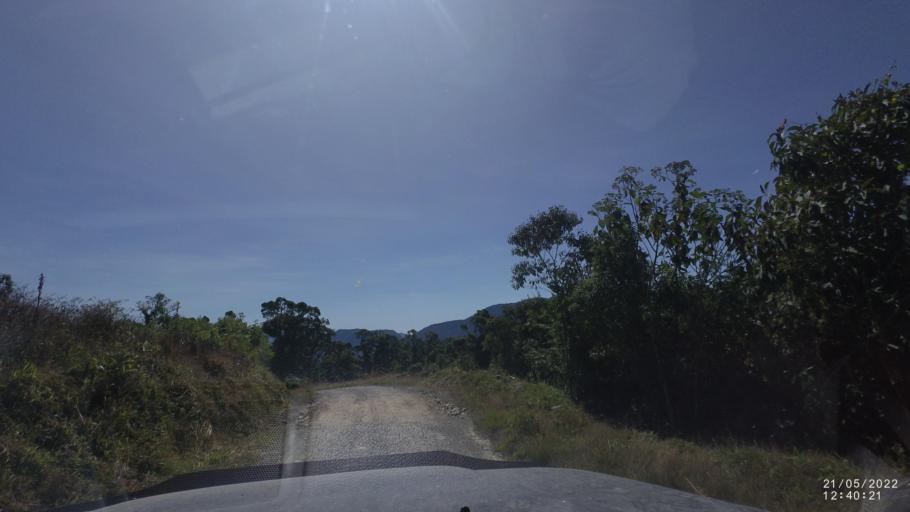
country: BO
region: Cochabamba
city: Colomi
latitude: -17.1968
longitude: -65.9255
